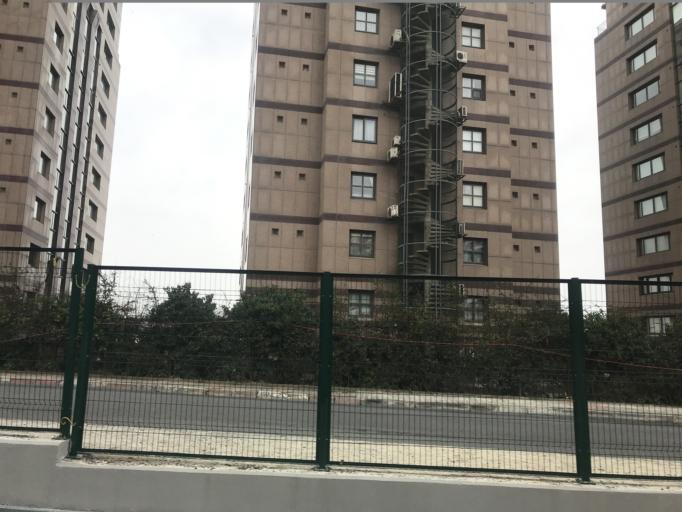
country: TR
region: Istanbul
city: Adalar
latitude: 40.8898
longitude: 29.1776
